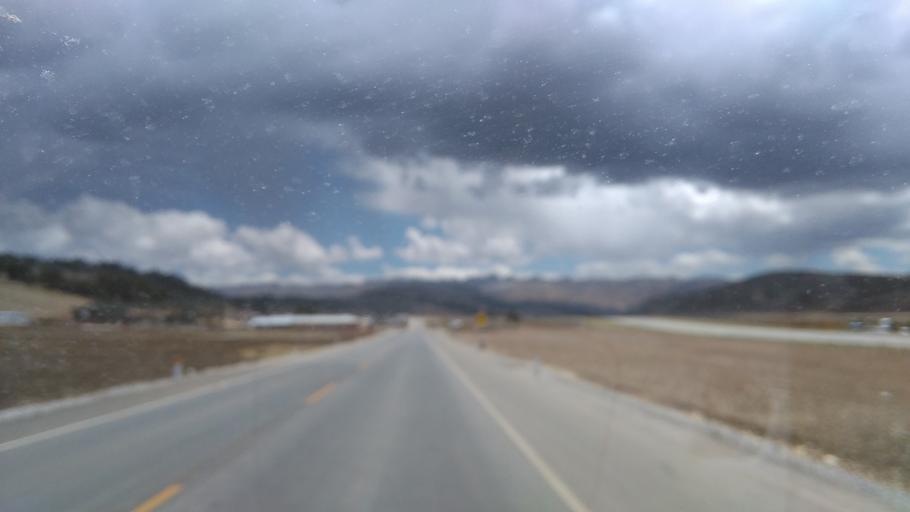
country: PE
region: Apurimac
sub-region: Provincia de Andahuaylas
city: San Jeronimo
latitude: -13.7038
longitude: -73.3468
